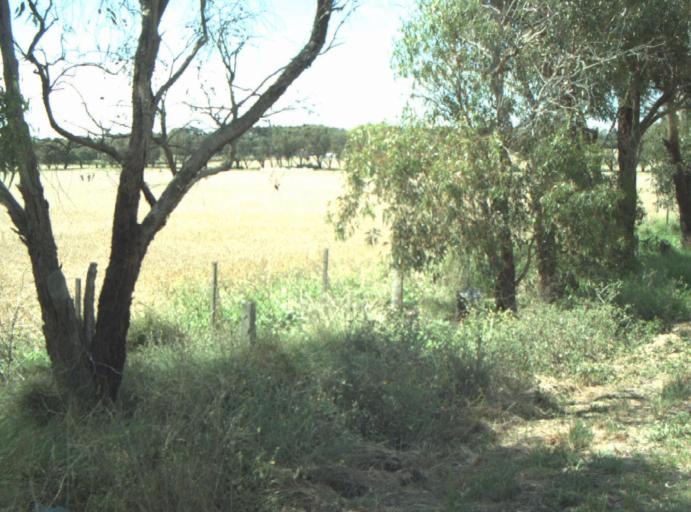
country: AU
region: Victoria
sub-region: Greater Geelong
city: Leopold
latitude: -38.1659
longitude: 144.4728
